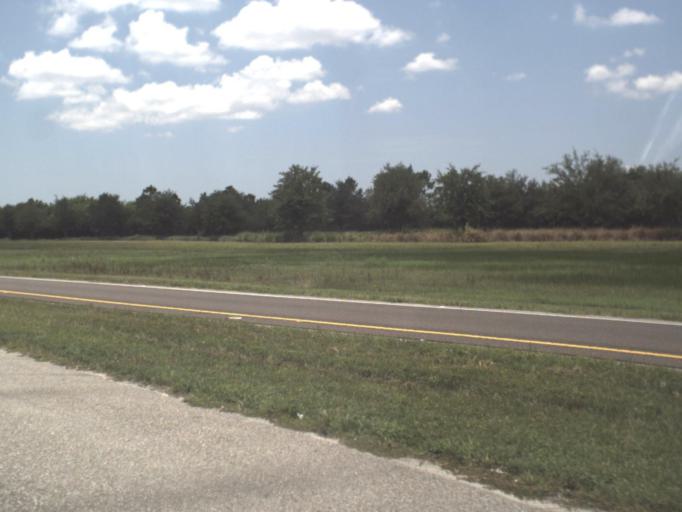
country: US
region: Florida
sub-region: Pinellas County
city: Feather Sound
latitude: 27.8900
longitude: -82.6488
